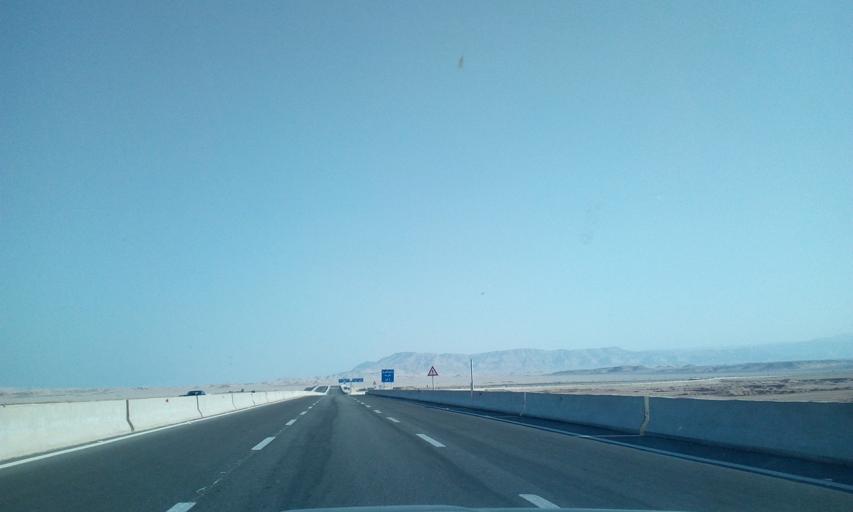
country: EG
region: As Suways
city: Ain Sukhna
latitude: 29.1172
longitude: 32.5297
